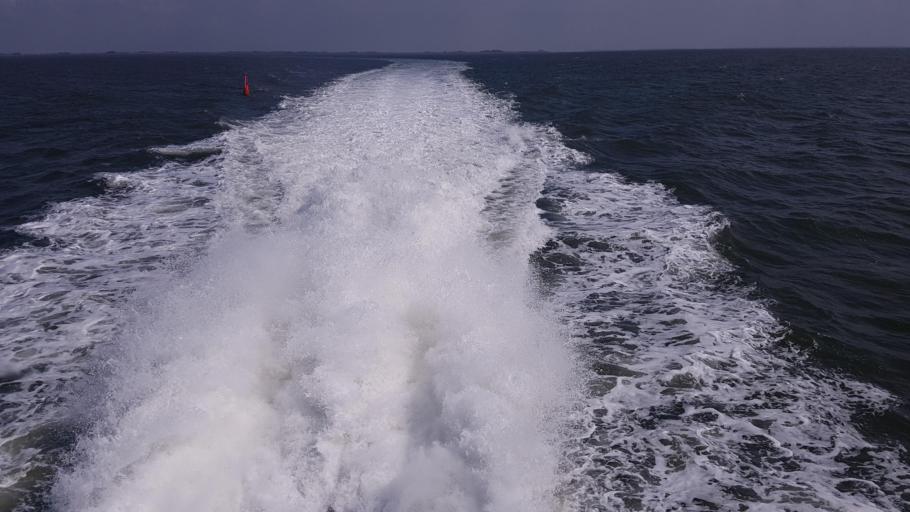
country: DE
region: Schleswig-Holstein
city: Pellworm
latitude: 54.4857
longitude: 8.7408
